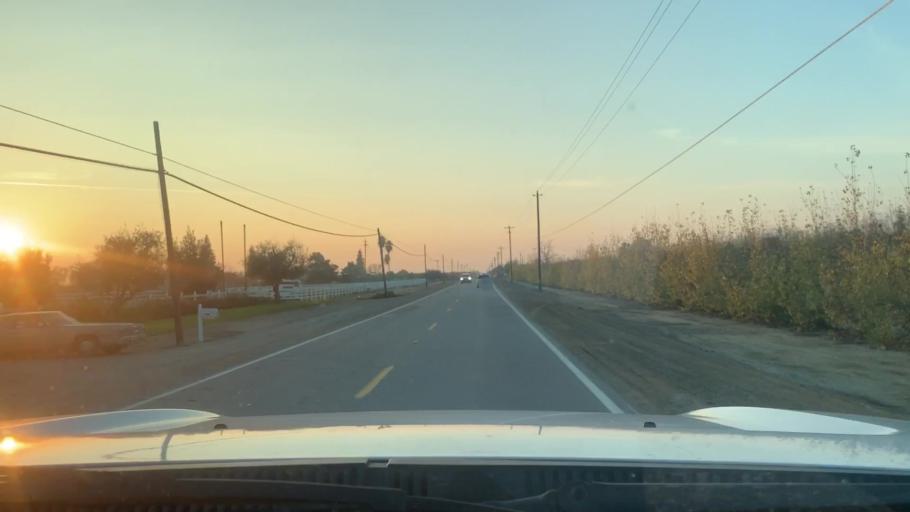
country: US
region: California
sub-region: Kern County
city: Rosedale
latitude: 35.3835
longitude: -119.2115
